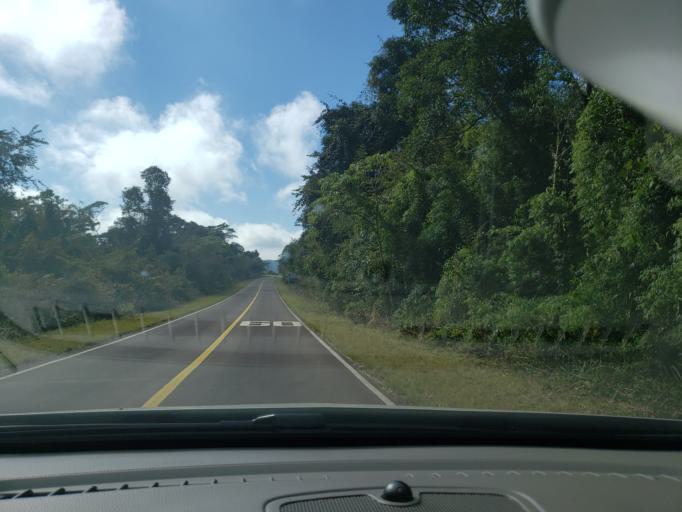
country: AR
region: Misiones
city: El Soberbio
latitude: -27.1249
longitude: -53.9501
